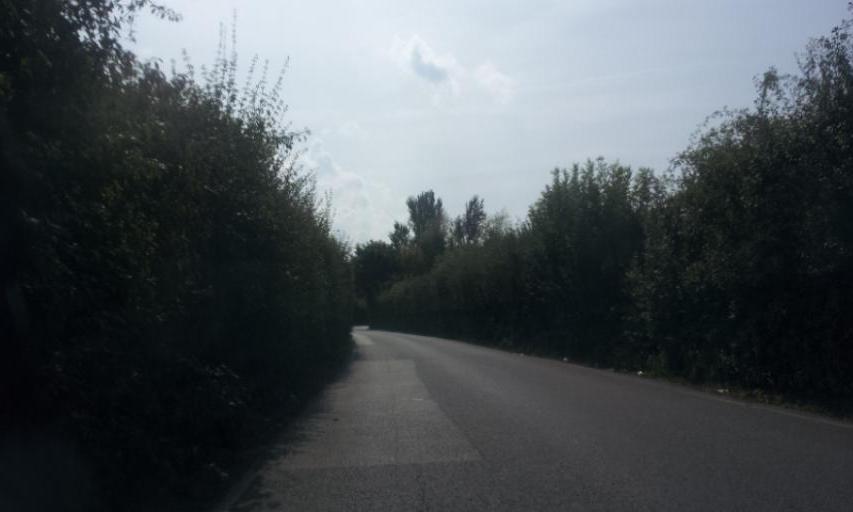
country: GB
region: England
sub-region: Kent
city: Paddock Wood
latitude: 51.1701
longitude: 0.4014
